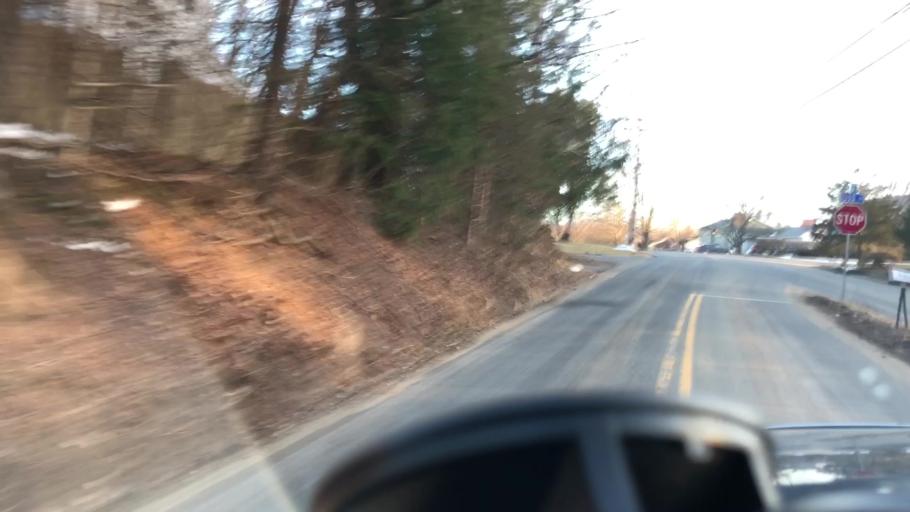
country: US
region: Massachusetts
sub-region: Hampshire County
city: Southampton
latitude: 42.2063
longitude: -72.6804
